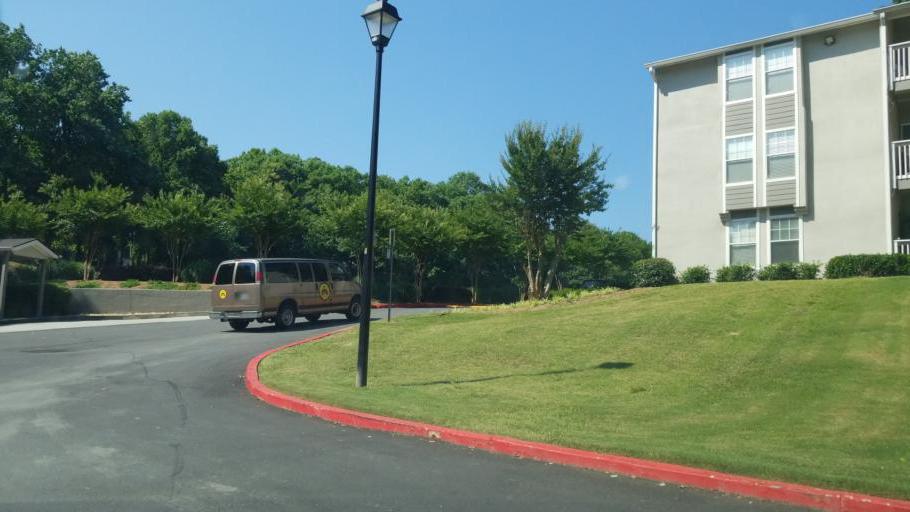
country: US
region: Georgia
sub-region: Cobb County
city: Vinings
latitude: 33.8921
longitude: -84.4717
